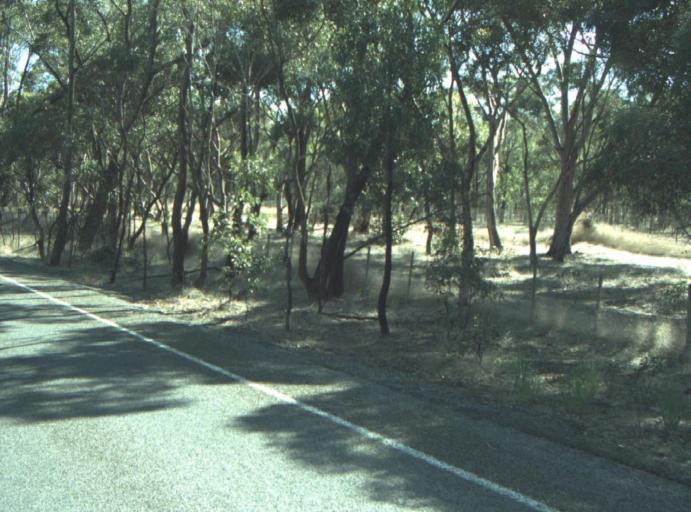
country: AU
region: Victoria
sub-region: Greater Geelong
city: Lara
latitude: -37.9189
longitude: 144.3968
